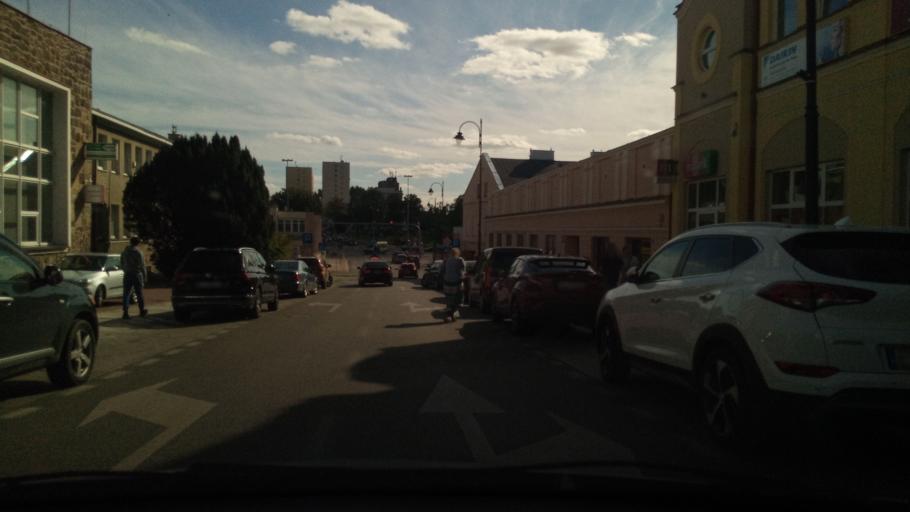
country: PL
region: Lodz Voivodeship
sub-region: Piotrkow Trybunalski
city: Piotrkow Trybunalski
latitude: 51.4082
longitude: 19.6886
